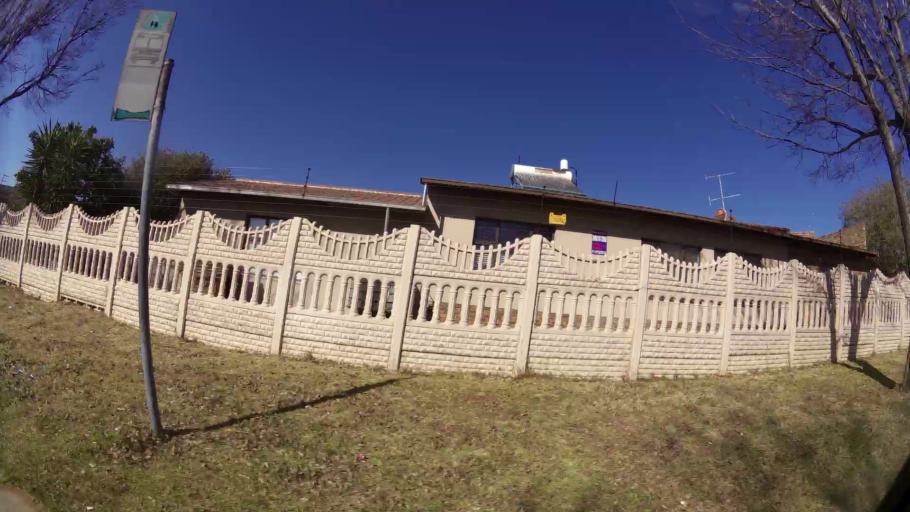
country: ZA
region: Gauteng
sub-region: Ekurhuleni Metropolitan Municipality
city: Germiston
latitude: -26.2427
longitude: 28.1101
